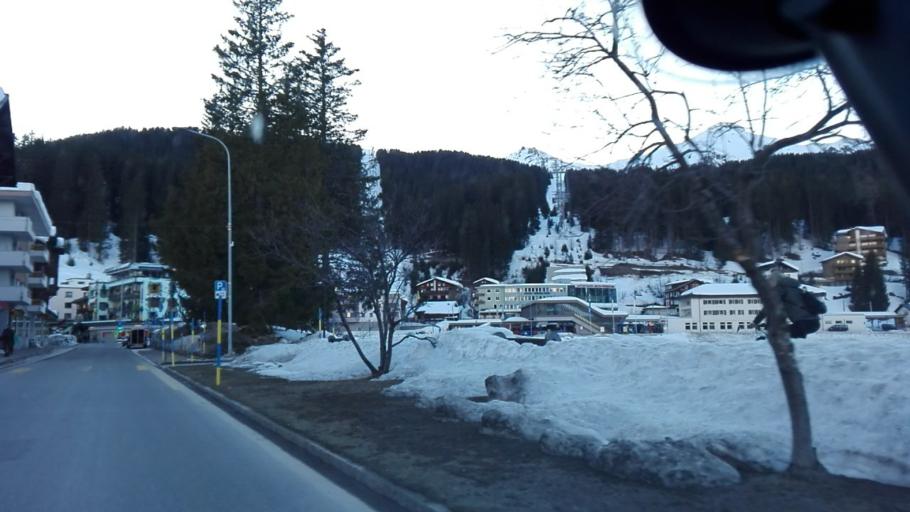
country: CH
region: Grisons
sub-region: Plessur District
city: Arosa
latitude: 46.7829
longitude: 9.6820
